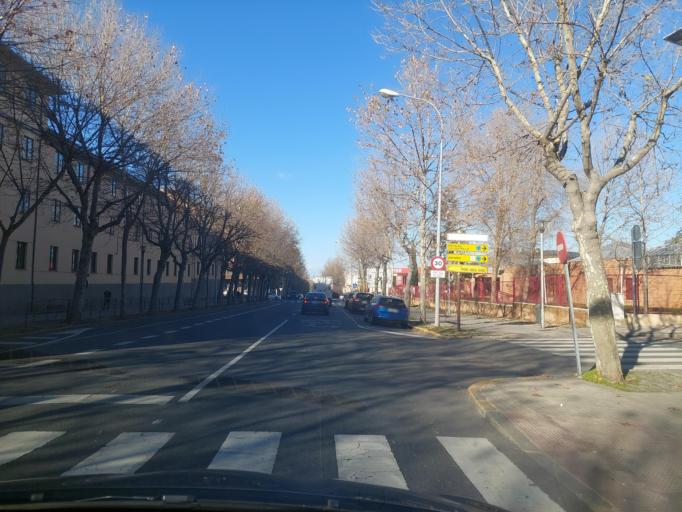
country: ES
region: Castille and Leon
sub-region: Provincia de Segovia
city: Segovia
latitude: 40.9366
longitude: -4.1106
